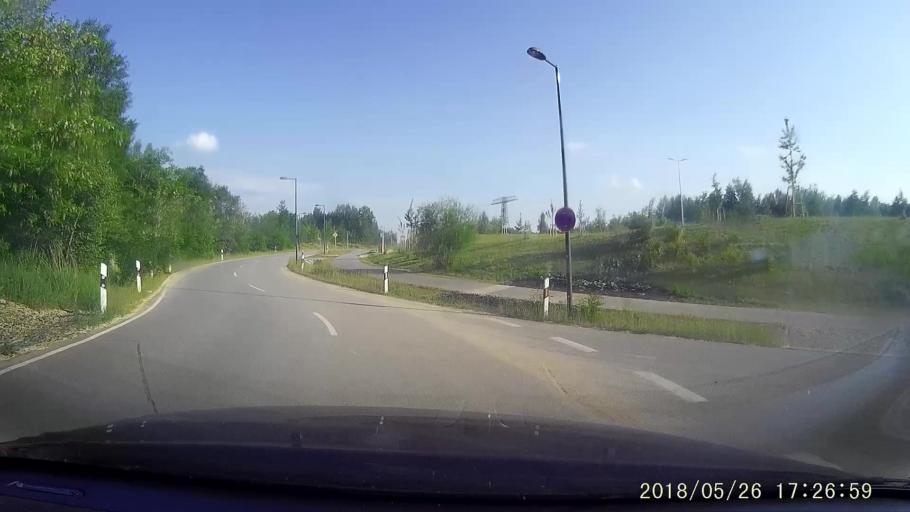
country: DE
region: Saxony
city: Ostritz
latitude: 51.0723
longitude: 14.9565
